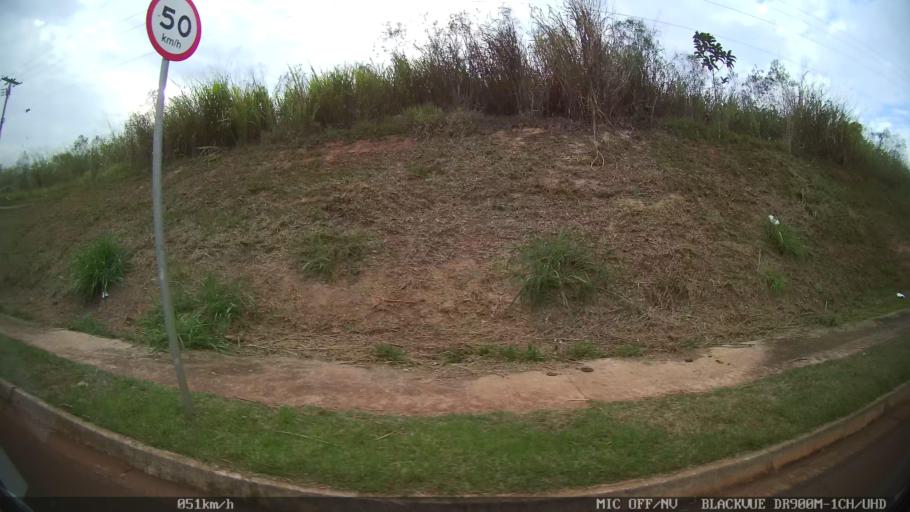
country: BR
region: Sao Paulo
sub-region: Americana
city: Americana
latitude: -22.6510
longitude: -47.3484
